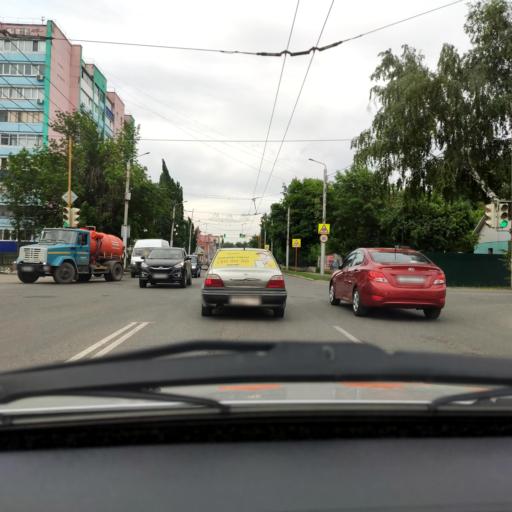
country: RU
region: Bashkortostan
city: Sterlitamak
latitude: 53.6170
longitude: 55.9588
